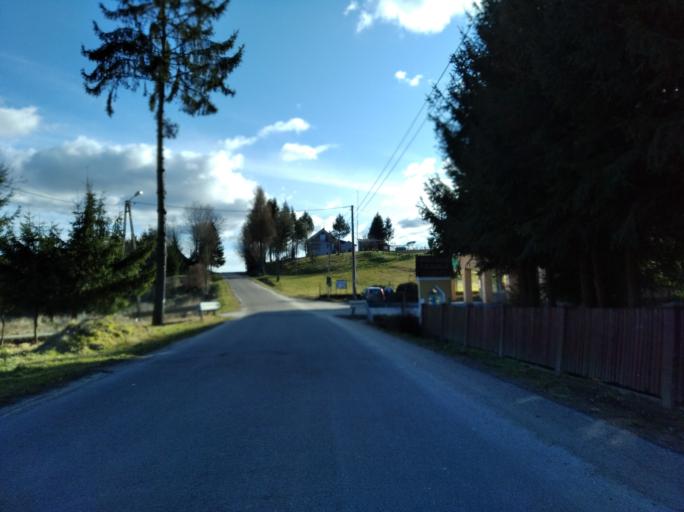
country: PL
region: Subcarpathian Voivodeship
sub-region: Powiat strzyzowski
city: Wisniowa
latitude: 49.8881
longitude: 21.7146
